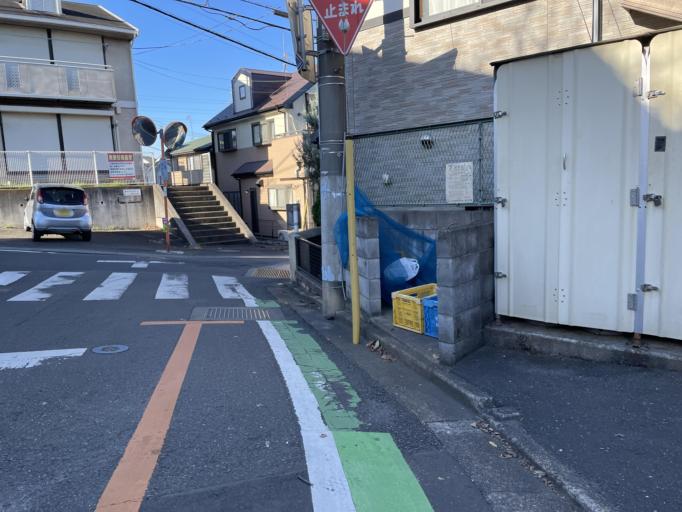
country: JP
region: Saitama
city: Wako
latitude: 35.7923
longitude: 139.6260
